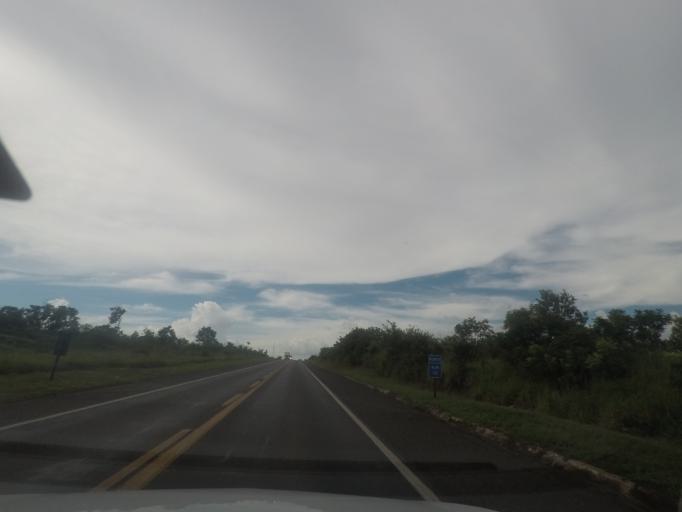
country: BR
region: Minas Gerais
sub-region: Prata
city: Prata
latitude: -19.3213
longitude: -48.9065
